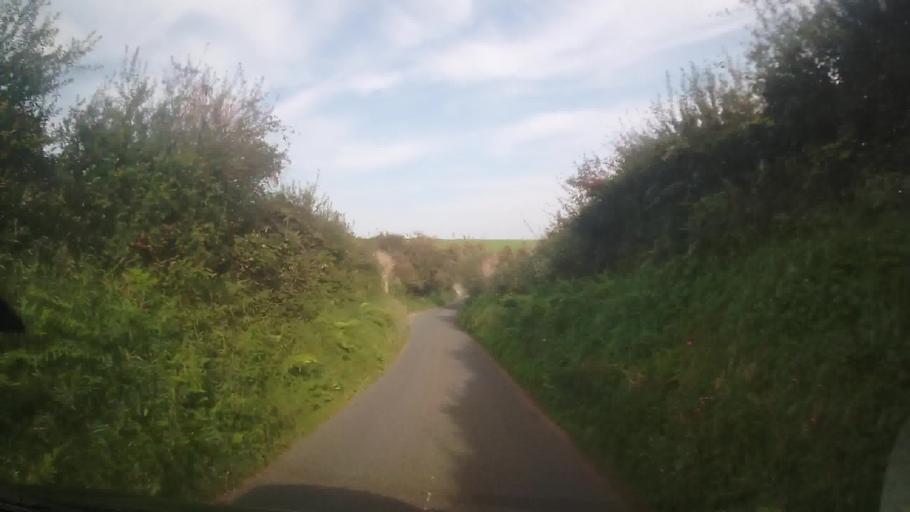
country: GB
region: Wales
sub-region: Pembrokeshire
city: Camrose
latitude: 51.8507
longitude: -5.0683
